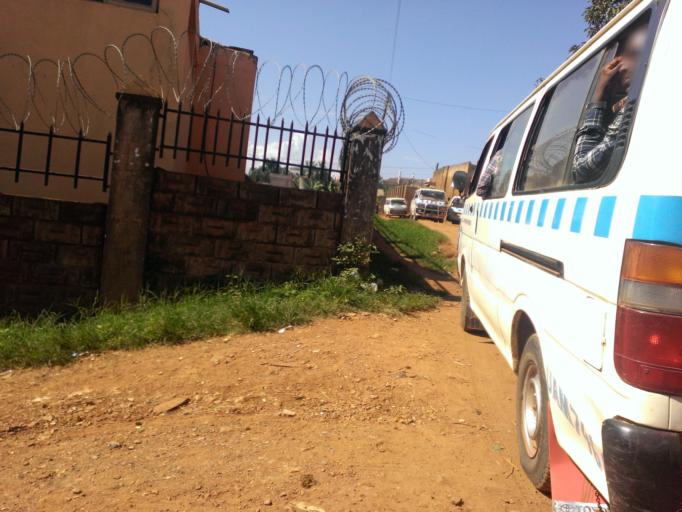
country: UG
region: Central Region
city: Kampala Central Division
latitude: 0.3241
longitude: 32.5645
